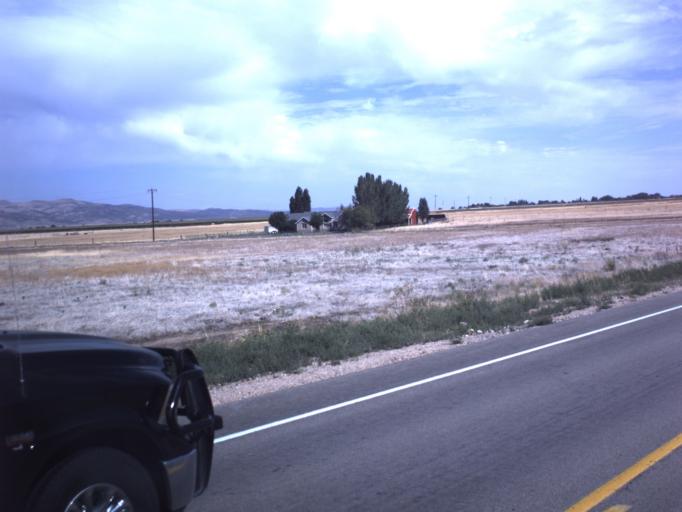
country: US
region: Utah
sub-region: Juab County
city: Nephi
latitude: 39.5274
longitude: -111.8658
